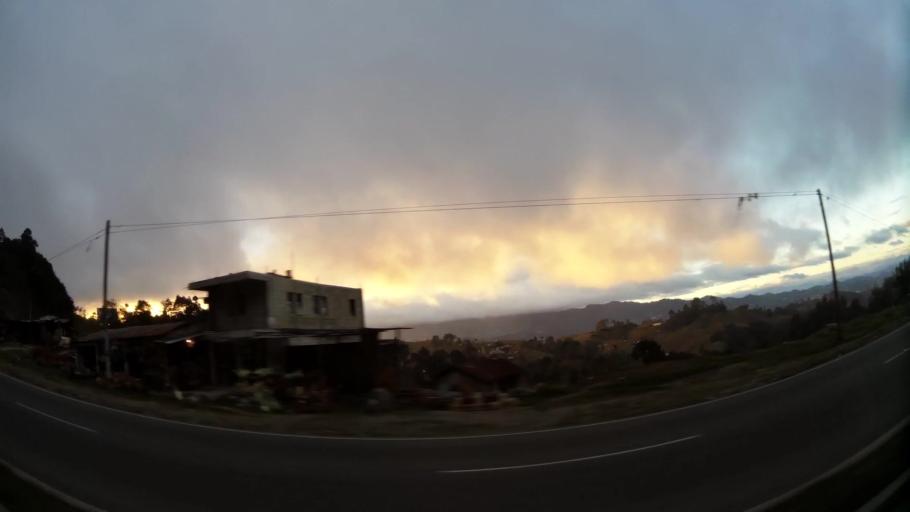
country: GT
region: Solola
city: Concepcion
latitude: 14.8493
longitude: -91.1362
